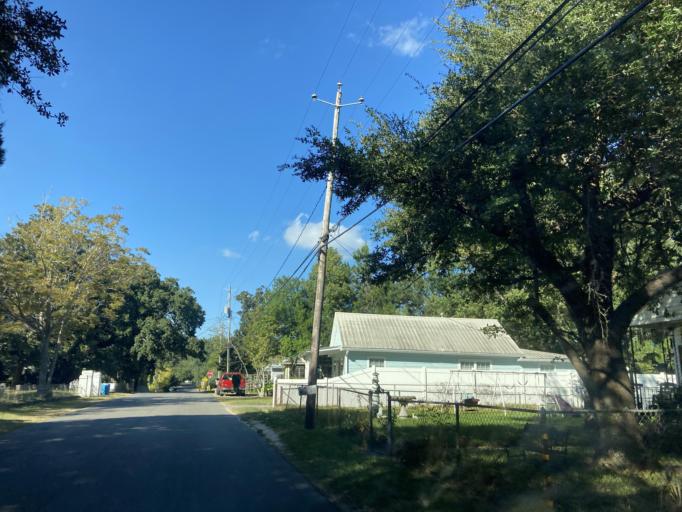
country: US
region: Mississippi
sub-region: Jackson County
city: Ocean Springs
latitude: 30.4081
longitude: -88.8264
